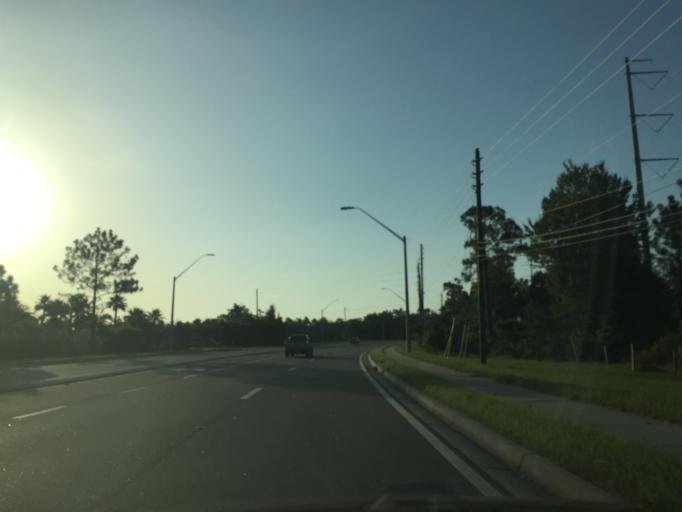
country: US
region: Florida
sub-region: Orange County
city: Alafaya
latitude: 28.5107
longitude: -81.1700
